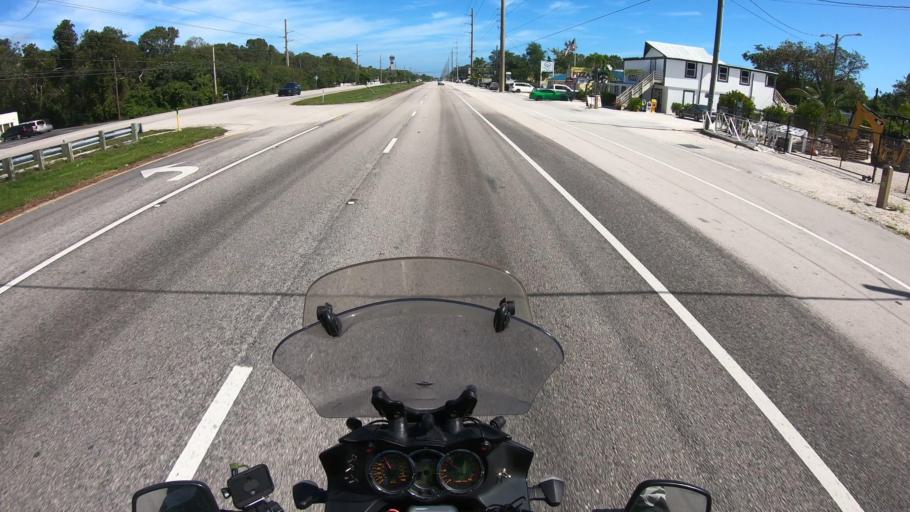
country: US
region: Florida
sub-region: Monroe County
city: Key Largo
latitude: 25.1157
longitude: -80.4213
